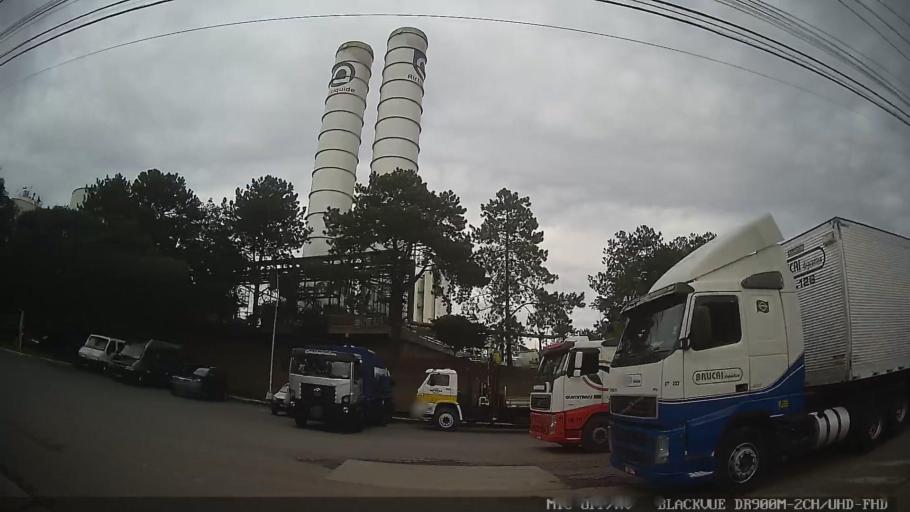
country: BR
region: Sao Paulo
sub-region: Maua
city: Maua
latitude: -23.6374
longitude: -46.4738
